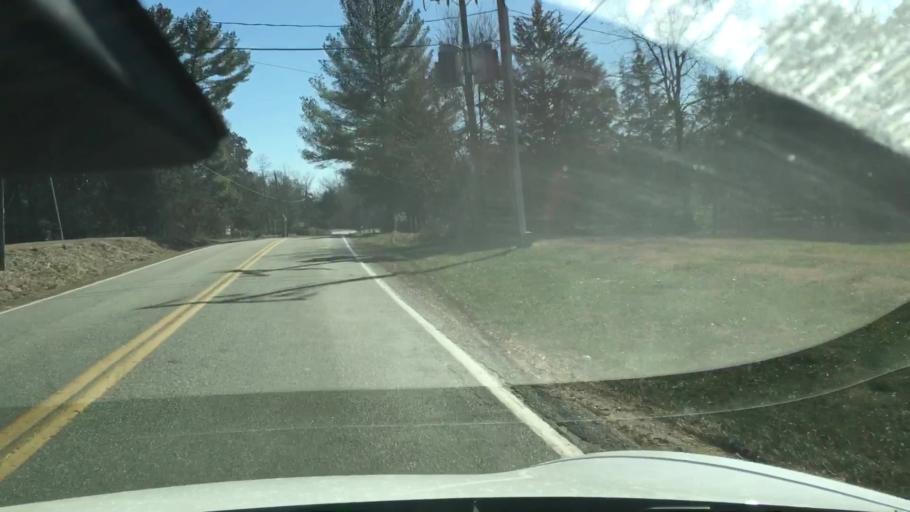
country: US
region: Virginia
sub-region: Henrico County
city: Short Pump
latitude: 37.5909
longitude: -77.7580
